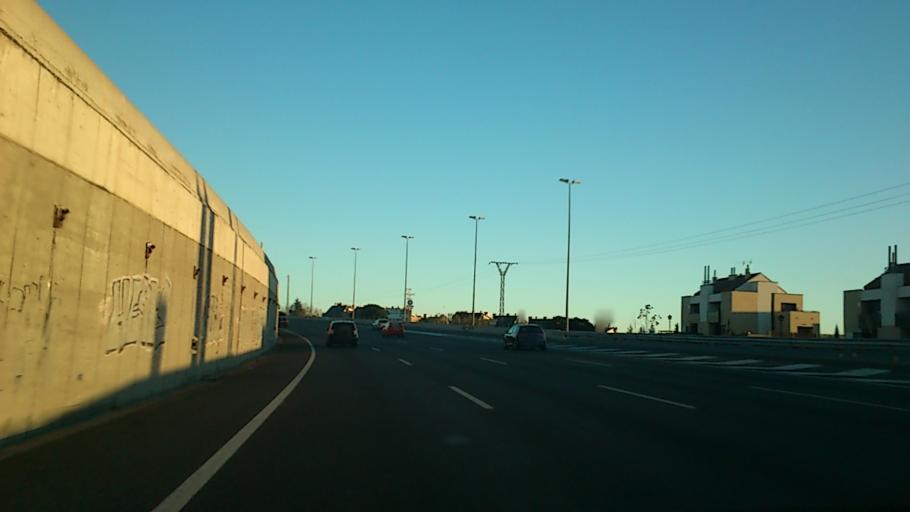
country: ES
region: Madrid
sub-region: Provincia de Madrid
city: Torrelodones
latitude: 40.5802
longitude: -3.9467
